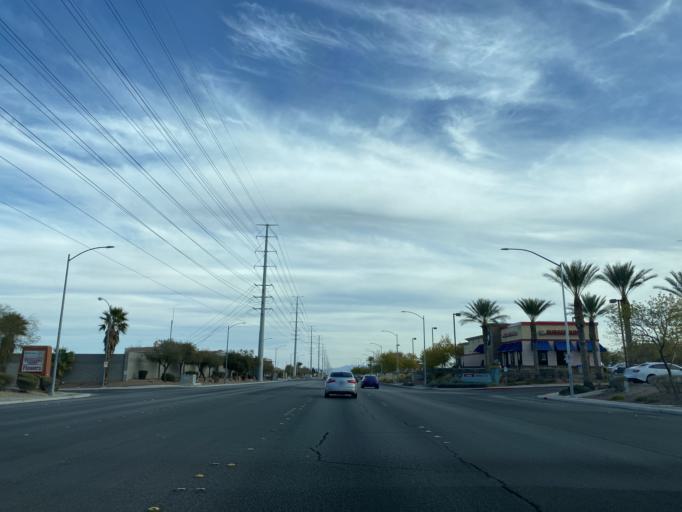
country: US
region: Nevada
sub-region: Clark County
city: Enterprise
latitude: 36.0555
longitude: -115.2776
